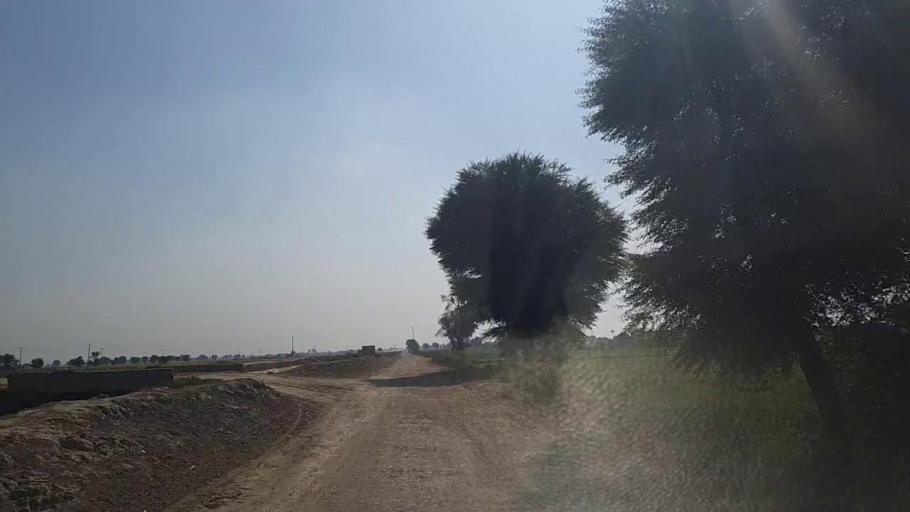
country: PK
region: Sindh
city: Shahpur Chakar
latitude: 26.2103
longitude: 68.5839
